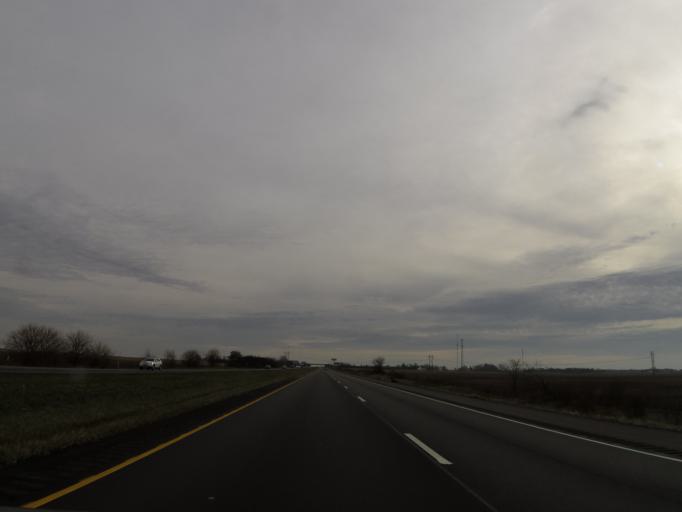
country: US
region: Indiana
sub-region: Montgomery County
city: Crawfordsville
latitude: 40.0966
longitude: -86.9946
